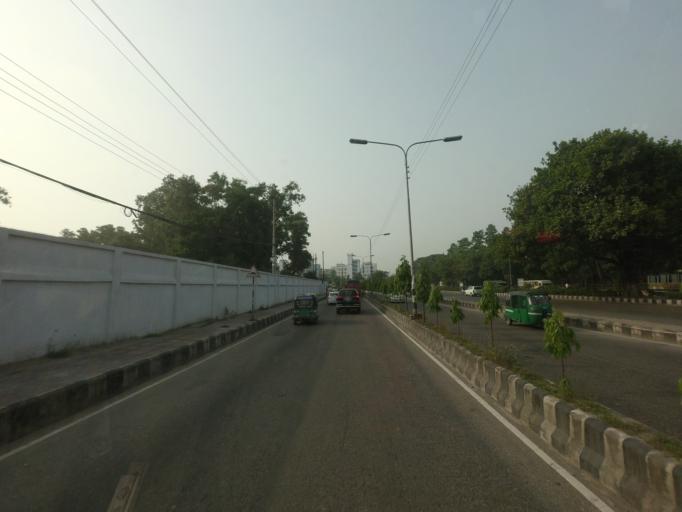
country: BD
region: Dhaka
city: Azimpur
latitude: 23.7667
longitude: 90.3833
